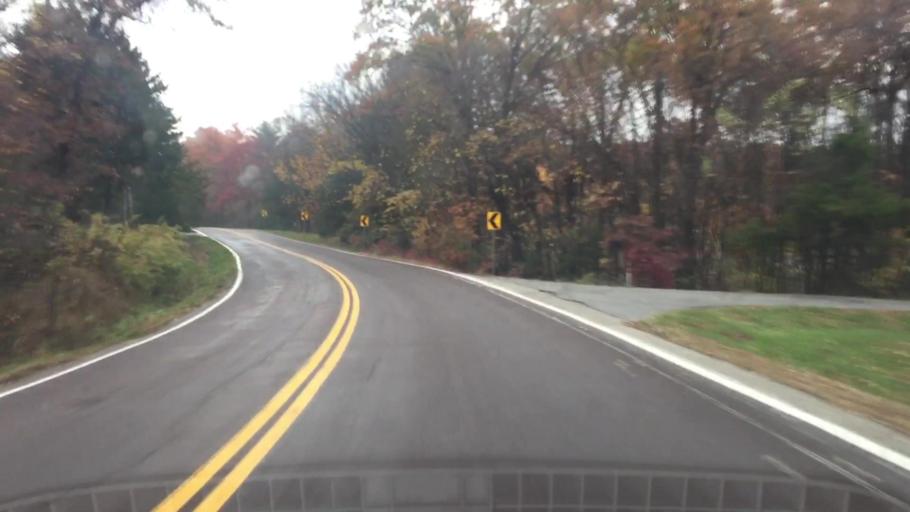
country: US
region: Missouri
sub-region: Boone County
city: Columbia
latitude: 38.8667
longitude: -92.3171
